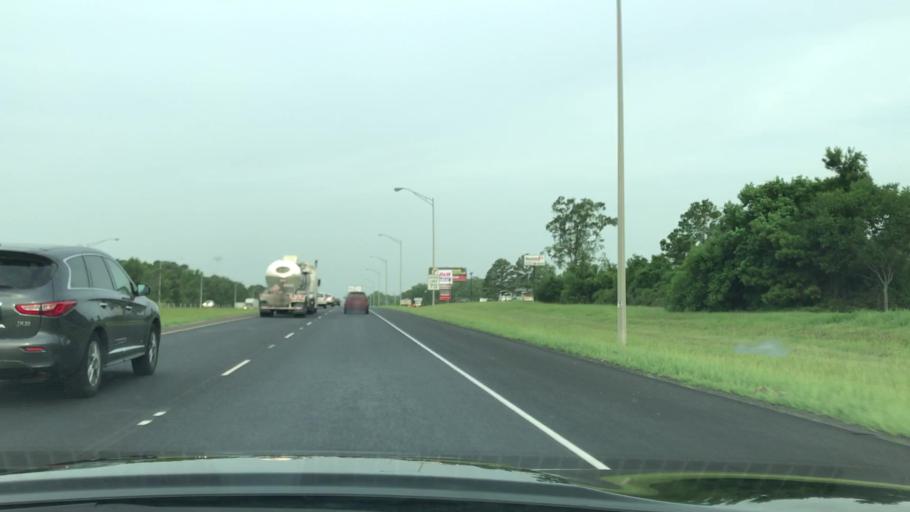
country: US
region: Louisiana
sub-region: Caddo Parish
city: Greenwood
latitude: 32.4493
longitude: -93.8808
